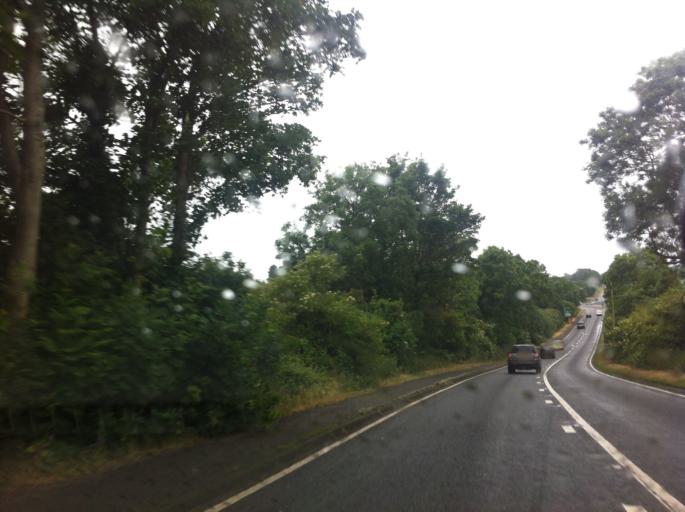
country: GB
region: England
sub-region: Northamptonshire
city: Irchester
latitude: 52.2611
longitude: -0.6776
